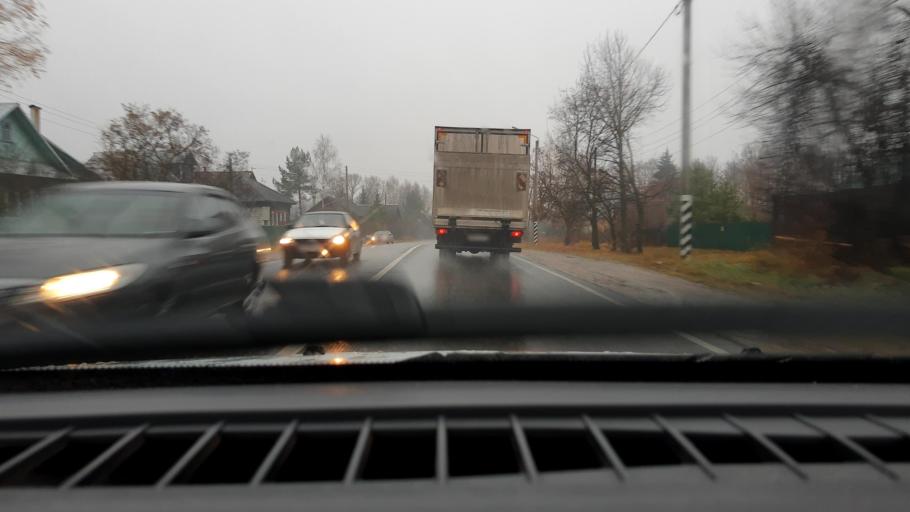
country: RU
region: Nizjnij Novgorod
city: Linda
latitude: 56.5690
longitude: 44.0246
